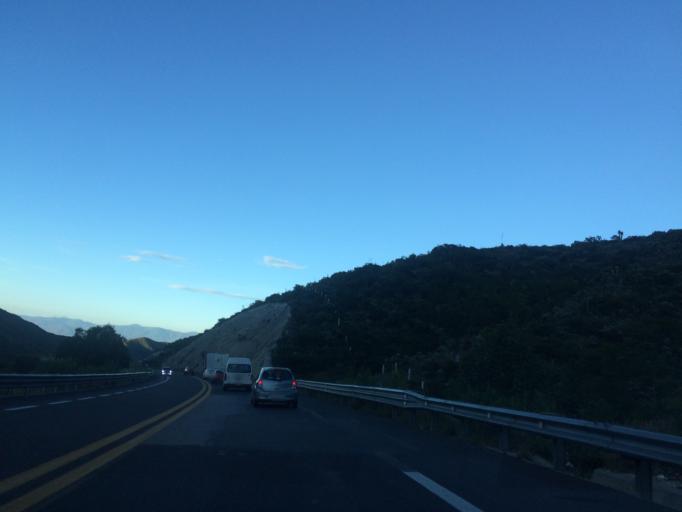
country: MX
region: Puebla
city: Chapuco
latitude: 18.6431
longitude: -97.4574
